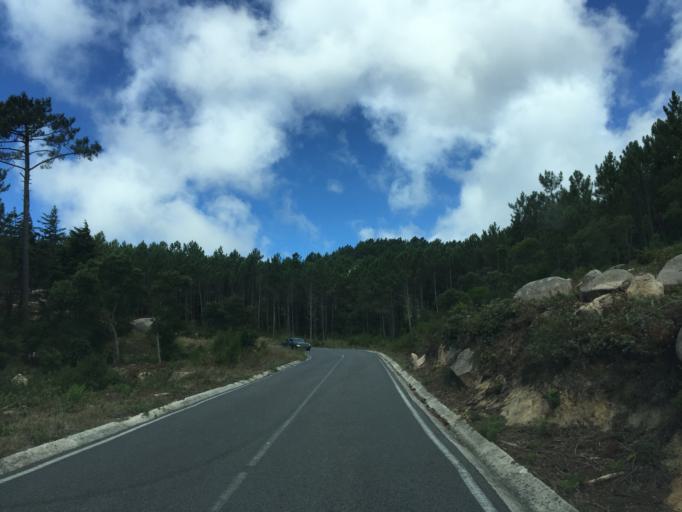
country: PT
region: Lisbon
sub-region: Cascais
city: Alcabideche
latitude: 38.7581
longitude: -9.4306
